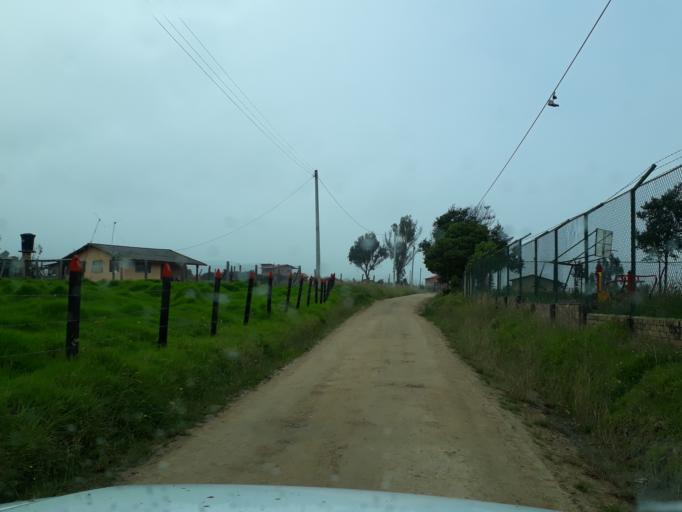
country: CO
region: Cundinamarca
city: Guasca
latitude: 4.8790
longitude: -73.8747
